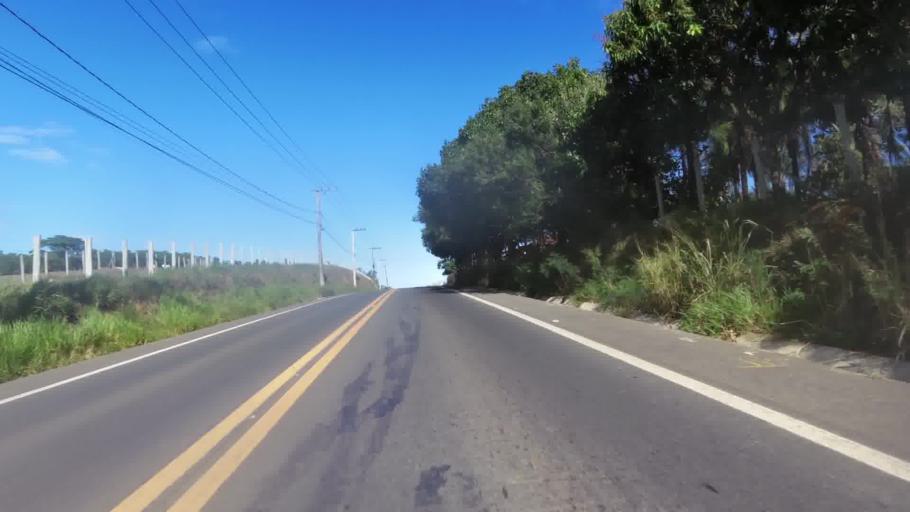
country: BR
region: Espirito Santo
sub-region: Piuma
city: Piuma
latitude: -20.8057
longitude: -40.6747
